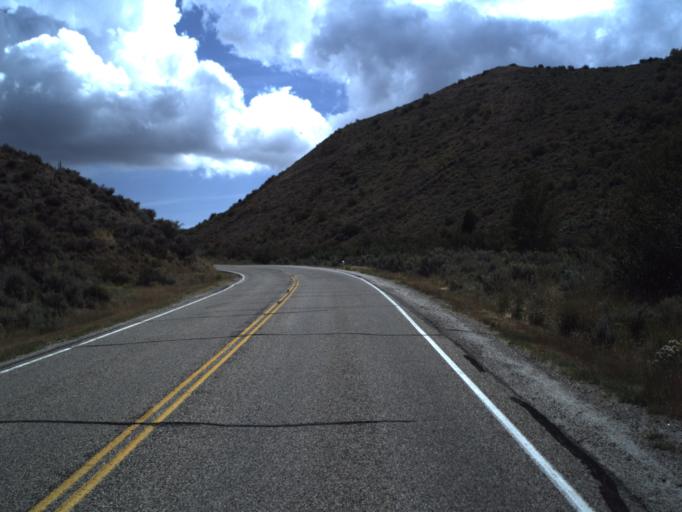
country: US
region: Utah
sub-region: Rich County
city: Randolph
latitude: 41.8193
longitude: -111.2823
